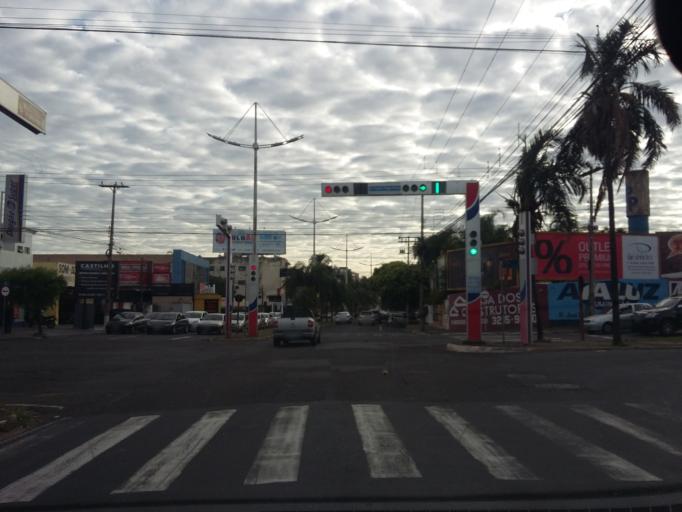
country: BR
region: Sao Paulo
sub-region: Sao Jose Do Rio Preto
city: Sao Jose do Rio Preto
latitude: -20.8333
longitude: -49.3997
